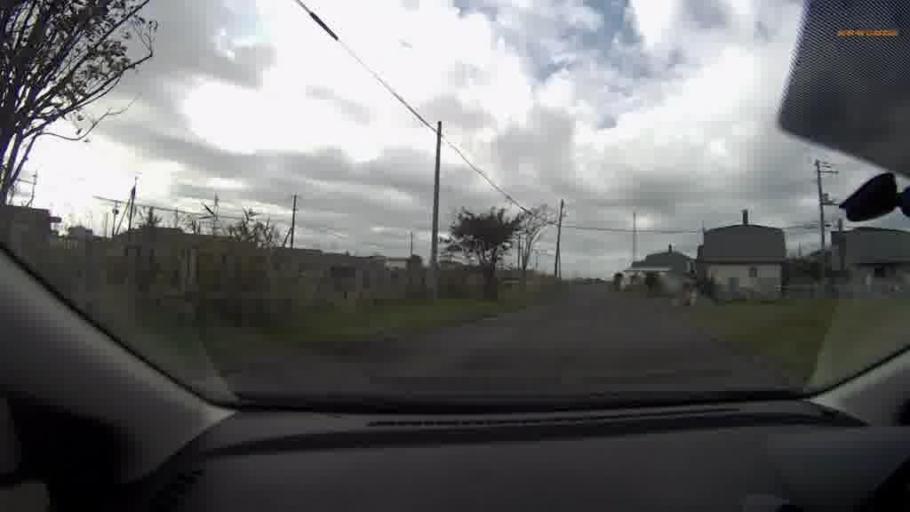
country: JP
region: Hokkaido
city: Kushiro
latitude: 42.9746
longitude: 144.1282
